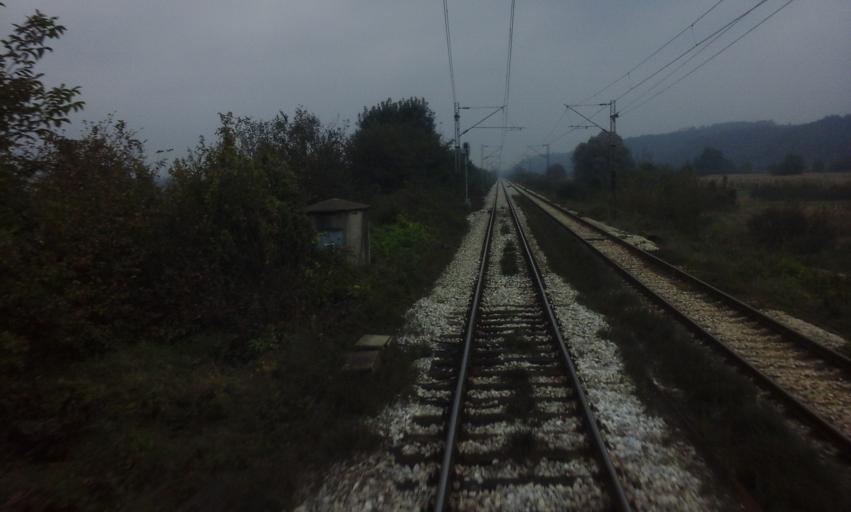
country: RS
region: Central Serbia
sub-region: Pomoravski Okrug
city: Jagodina
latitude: 44.0616
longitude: 21.2077
